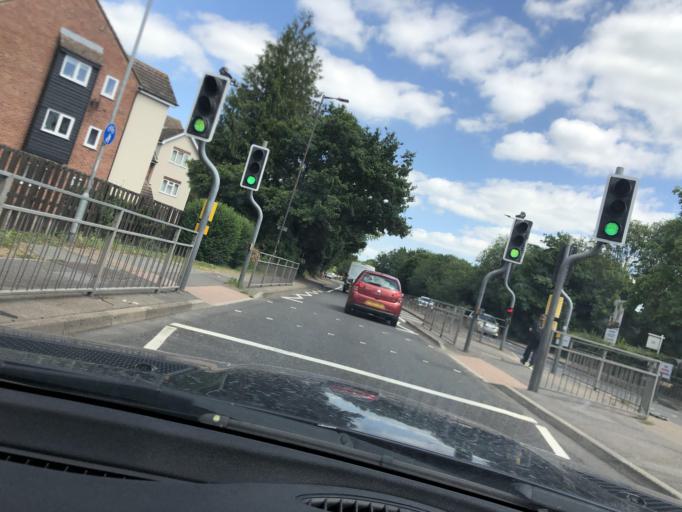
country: GB
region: England
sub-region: Essex
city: Chelmsford
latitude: 51.7218
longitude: 0.4613
